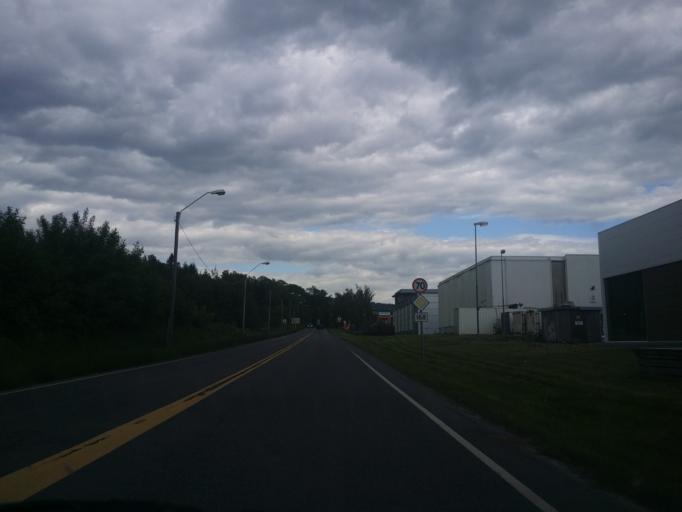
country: NO
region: Akershus
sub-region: Baerum
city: Lysaker
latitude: 59.9465
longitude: 10.5952
